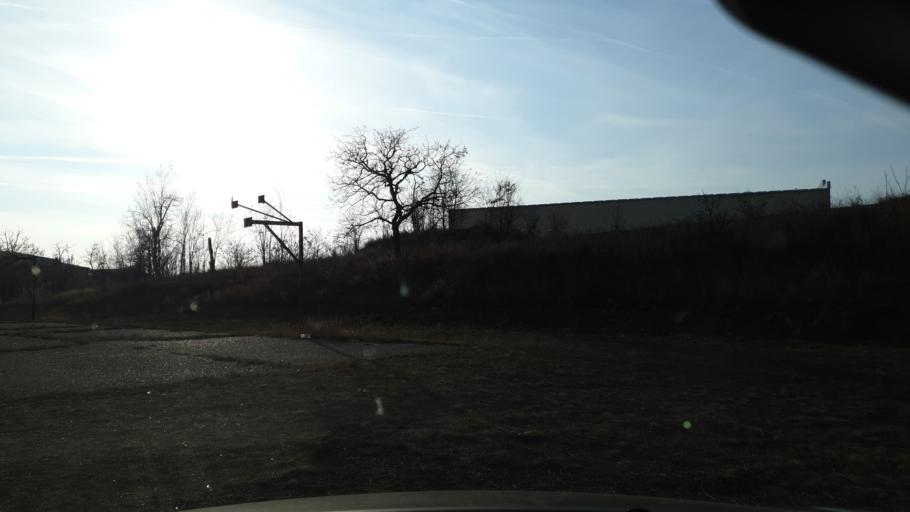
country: RS
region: Central Serbia
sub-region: Borski Okrug
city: Bor
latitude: 44.0535
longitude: 22.0988
